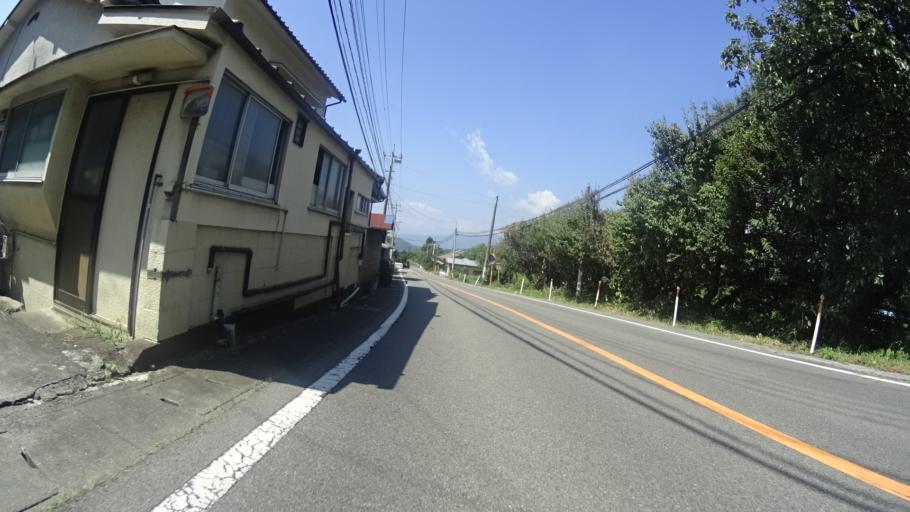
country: JP
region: Yamanashi
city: Enzan
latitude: 35.7264
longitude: 138.7580
